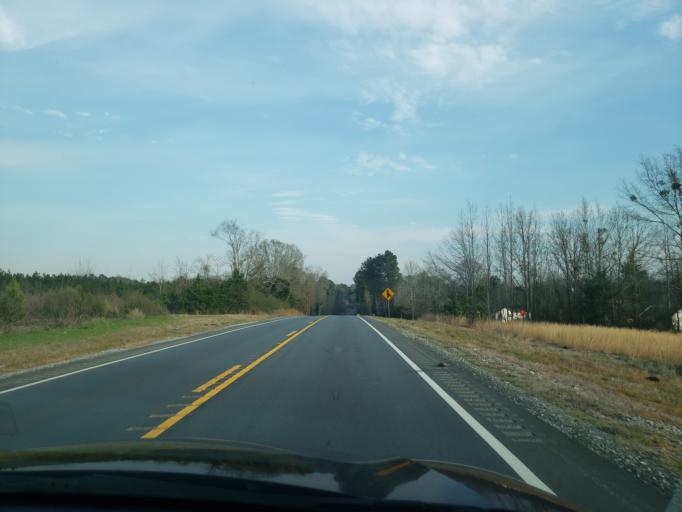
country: US
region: Alabama
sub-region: Hale County
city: Moundville
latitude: 32.8926
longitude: -87.6159
